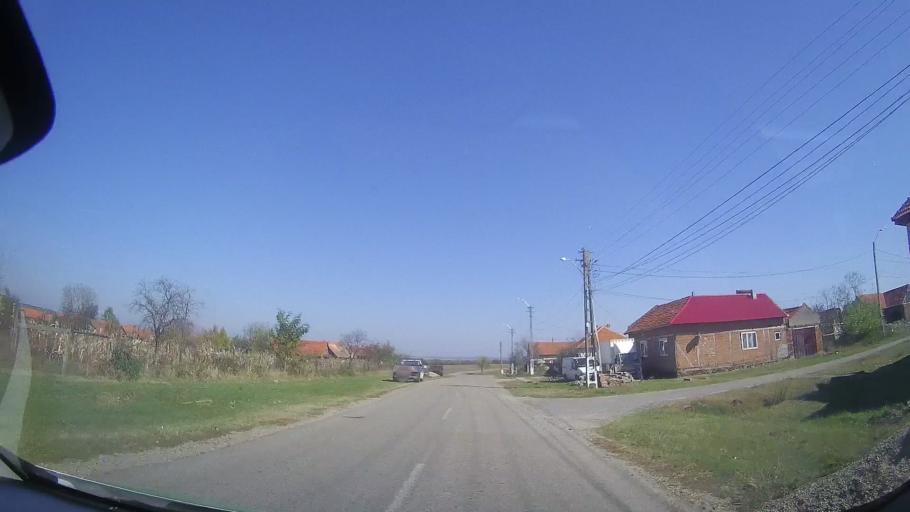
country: RO
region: Timis
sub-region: Comuna Bethausen
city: Bethausen
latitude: 45.8011
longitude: 21.9988
